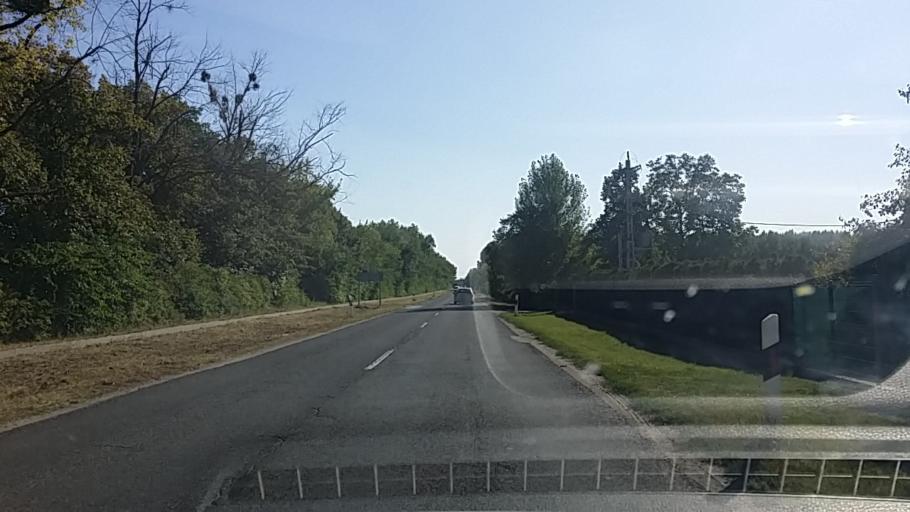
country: HU
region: Gyor-Moson-Sopron
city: Fertod
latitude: 47.6570
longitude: 16.8950
